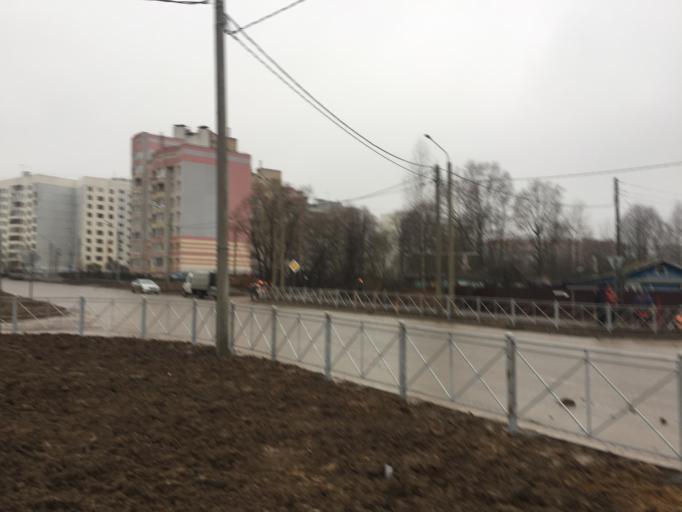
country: RU
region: Jaroslavl
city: Yaroslavl
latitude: 57.6972
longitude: 39.7848
